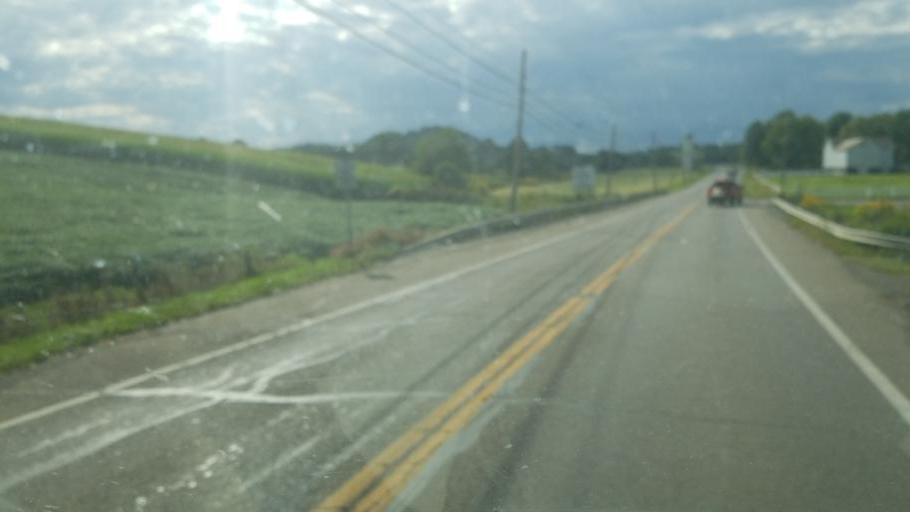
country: US
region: Ohio
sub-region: Tuscarawas County
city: Dover
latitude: 40.5096
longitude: -81.5328
